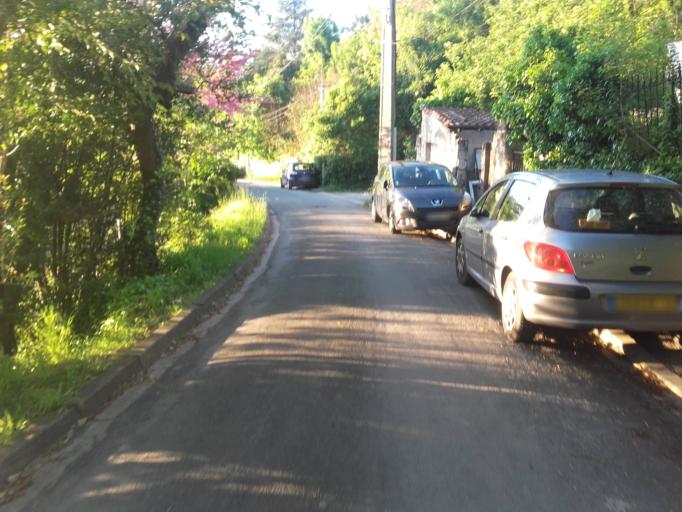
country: FR
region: Aquitaine
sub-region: Departement de la Gironde
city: Cenon
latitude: 44.8577
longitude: -0.5294
